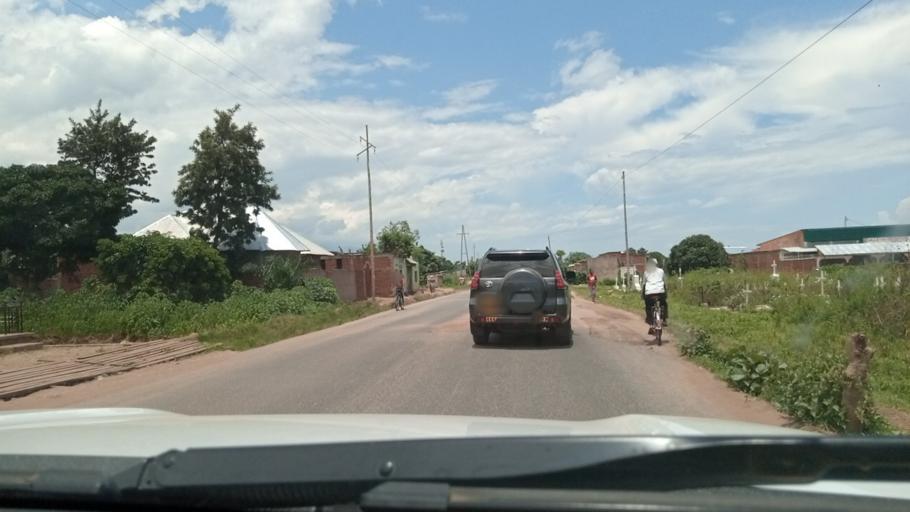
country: BI
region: Bujumbura Mairie
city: Bujumbura
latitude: -3.4650
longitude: 29.3501
